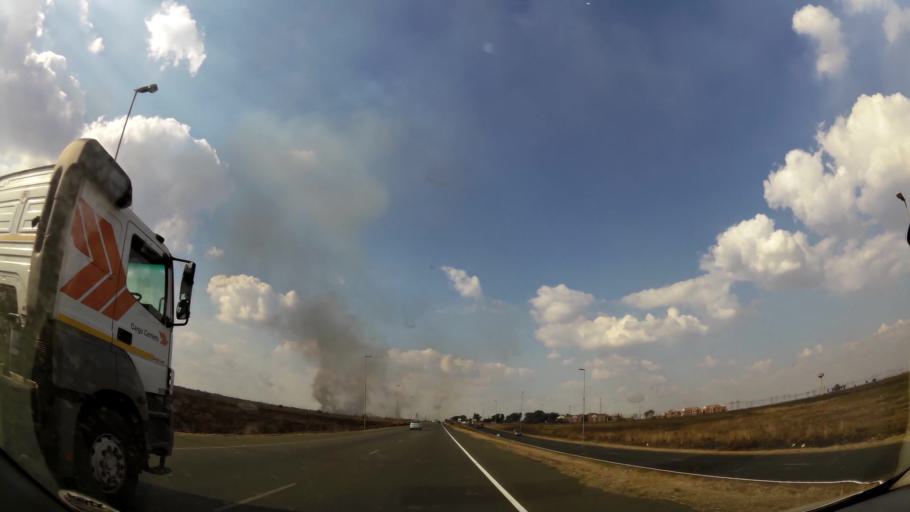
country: ZA
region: Gauteng
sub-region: Ekurhuleni Metropolitan Municipality
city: Boksburg
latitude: -26.2775
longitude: 28.2670
